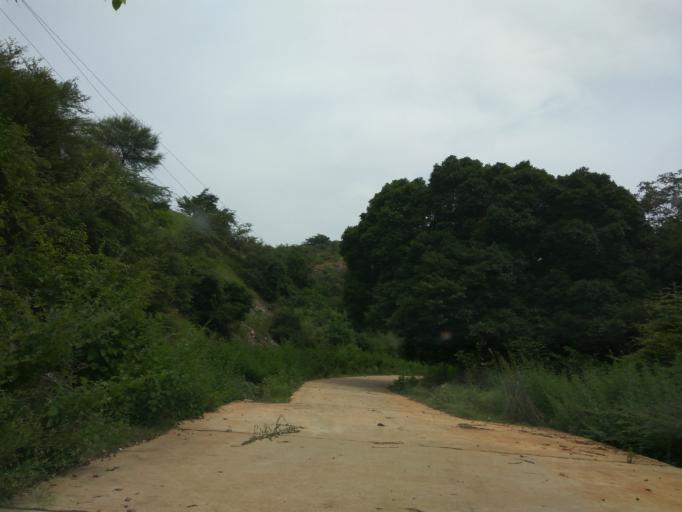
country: IN
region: Andhra Pradesh
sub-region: Prakasam
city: Cumbum
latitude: 15.4428
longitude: 79.0835
